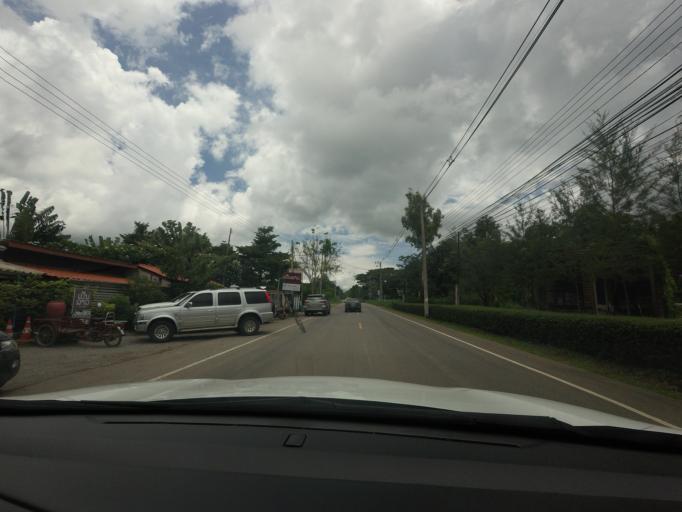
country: TH
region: Sara Buri
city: Muak Lek
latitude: 14.5437
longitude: 101.3344
